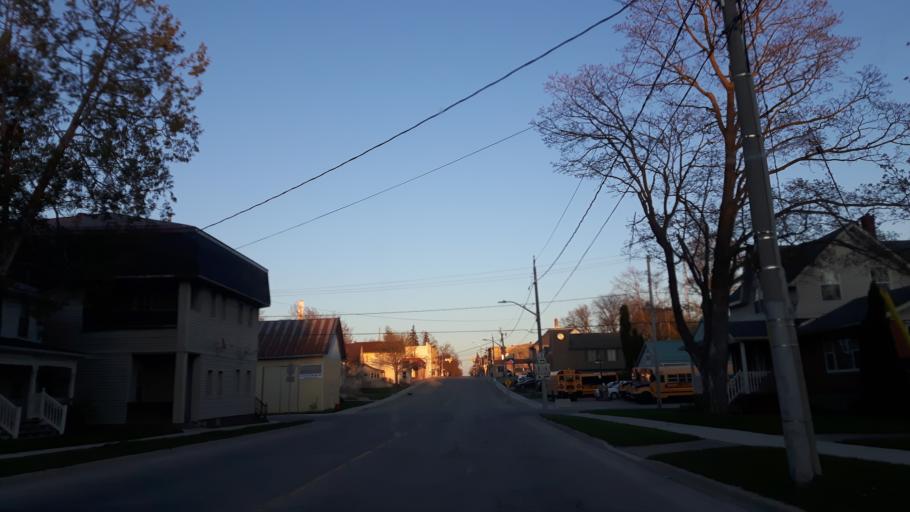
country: CA
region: Ontario
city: Bluewater
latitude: 43.6184
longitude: -81.5427
